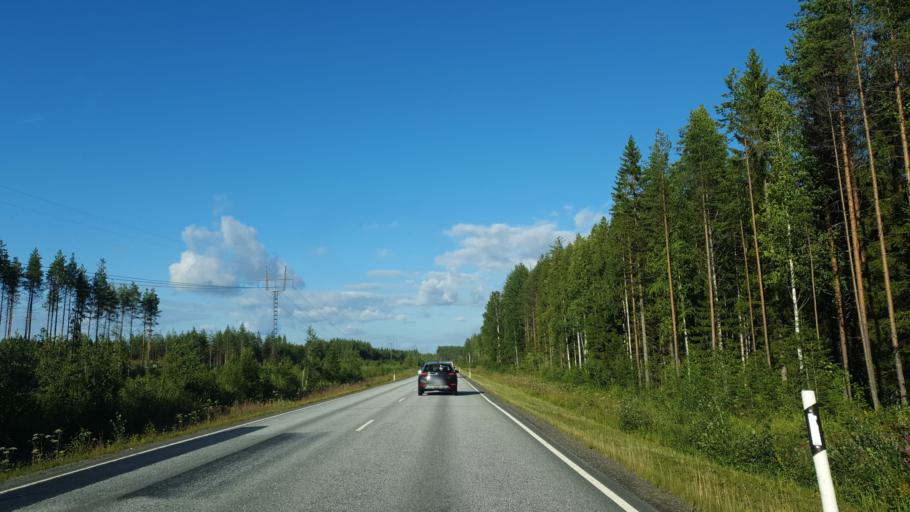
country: FI
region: North Karelia
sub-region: Joensuu
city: Outokumpu
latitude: 62.5317
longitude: 29.0911
